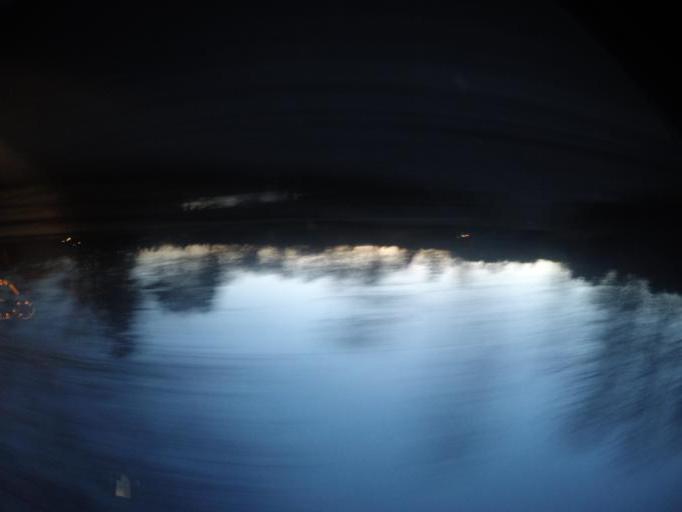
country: SE
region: Vaestmanland
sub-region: Arboga Kommun
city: Arboga
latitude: 59.4081
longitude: 15.7358
